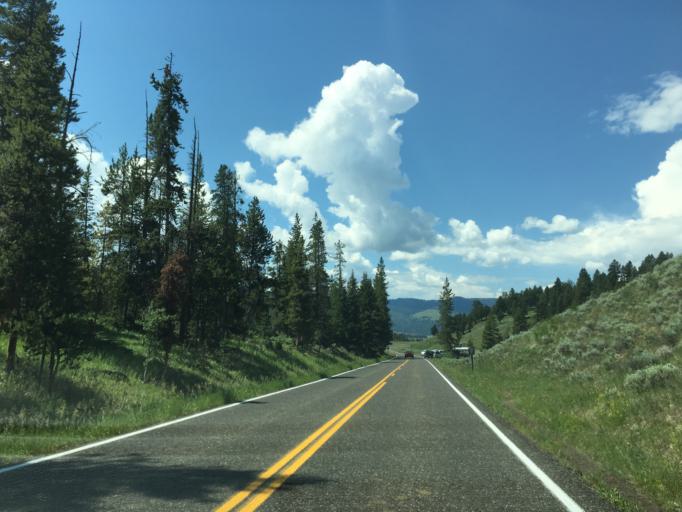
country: US
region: Montana
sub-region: Park County
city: Livingston
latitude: 44.9004
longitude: -110.1215
